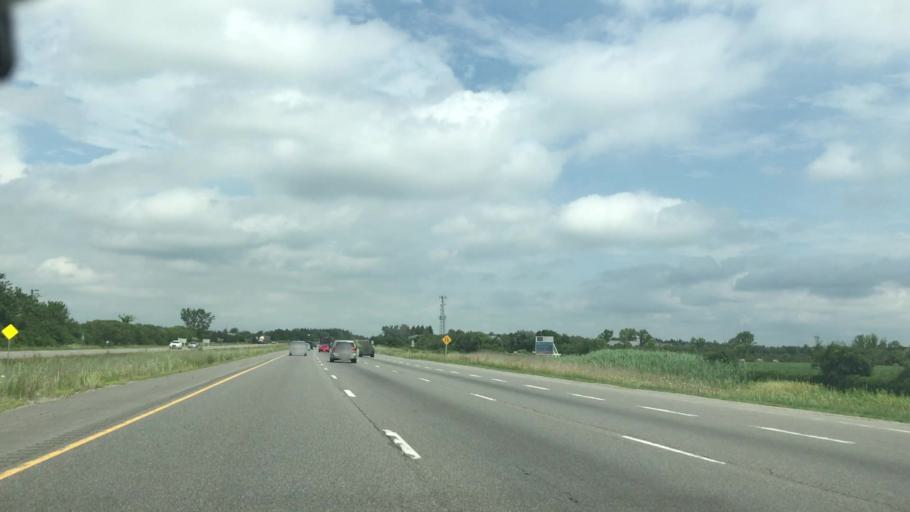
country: CA
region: Ontario
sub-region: York
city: Richmond Hill
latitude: 43.9471
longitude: -79.3906
